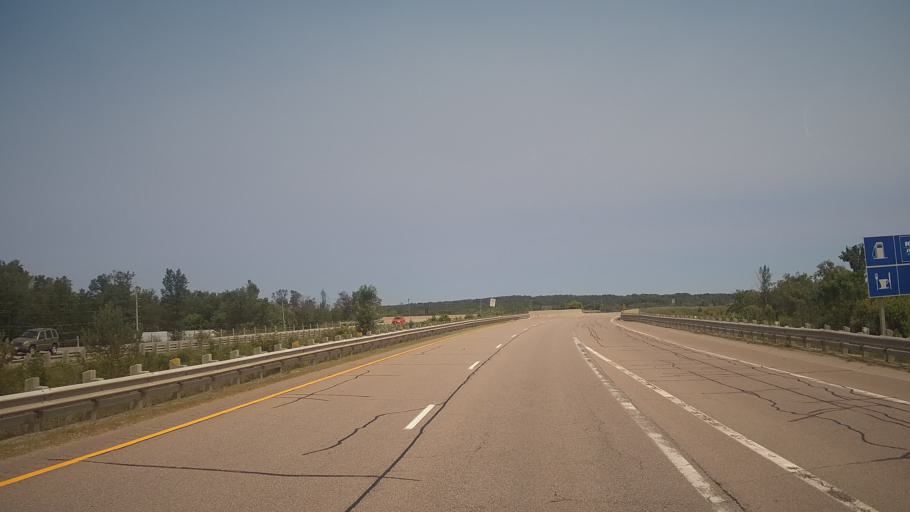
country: CA
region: Ontario
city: Midland
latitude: 44.7517
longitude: -79.7031
